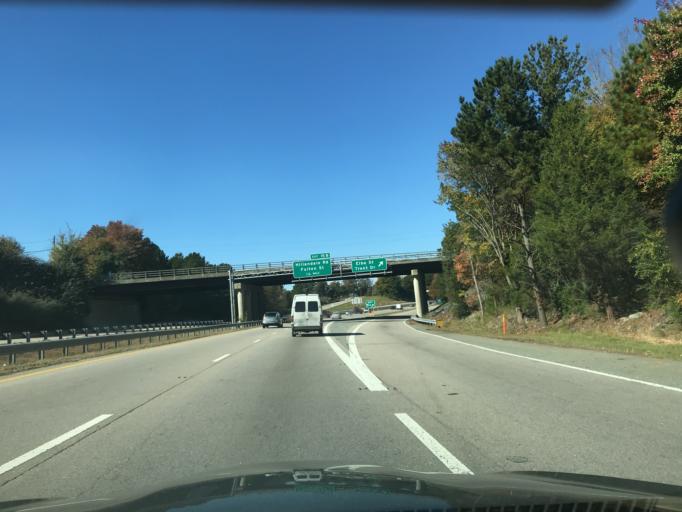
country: US
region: North Carolina
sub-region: Durham County
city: Durham
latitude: 36.0067
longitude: -78.9282
